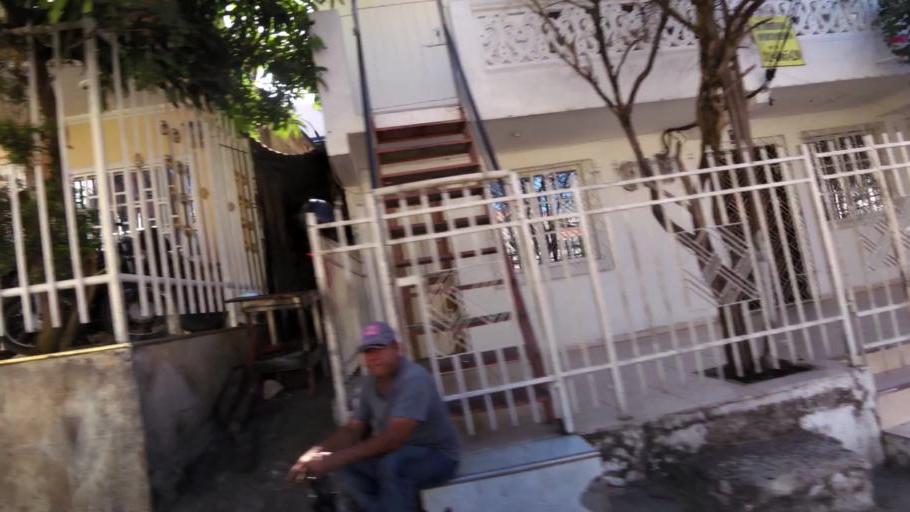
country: CO
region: Bolivar
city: Cartagena
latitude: 10.3951
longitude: -75.5093
